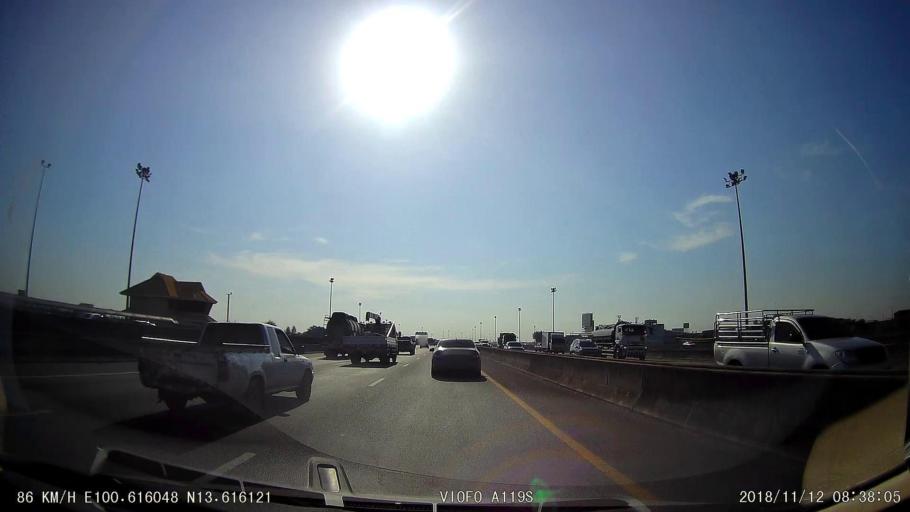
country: TH
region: Samut Prakan
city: Samut Prakan
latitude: 13.6162
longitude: 100.6159
